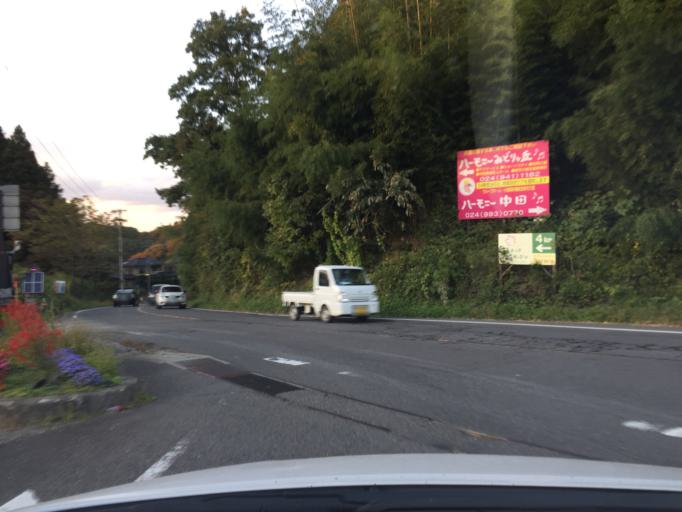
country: JP
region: Fukushima
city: Koriyama
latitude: 37.3652
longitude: 140.4486
